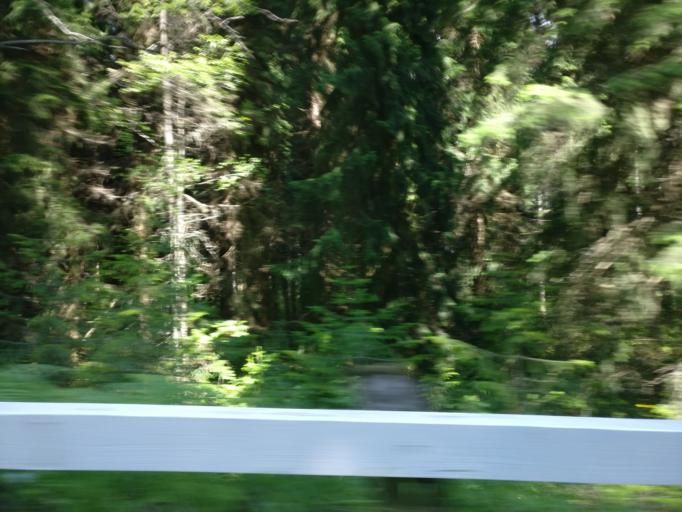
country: FI
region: Southern Savonia
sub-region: Savonlinna
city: Punkaharju
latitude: 61.8016
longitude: 29.3113
